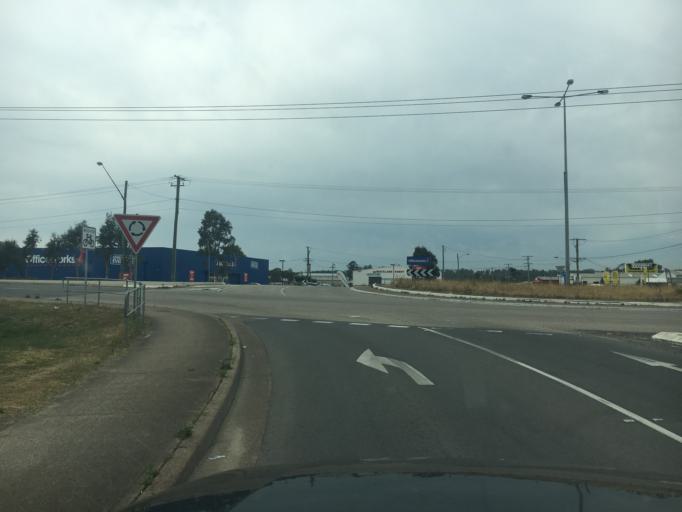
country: AU
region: New South Wales
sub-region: Maitland Municipality
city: Rutherford
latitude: -32.7105
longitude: 151.5169
